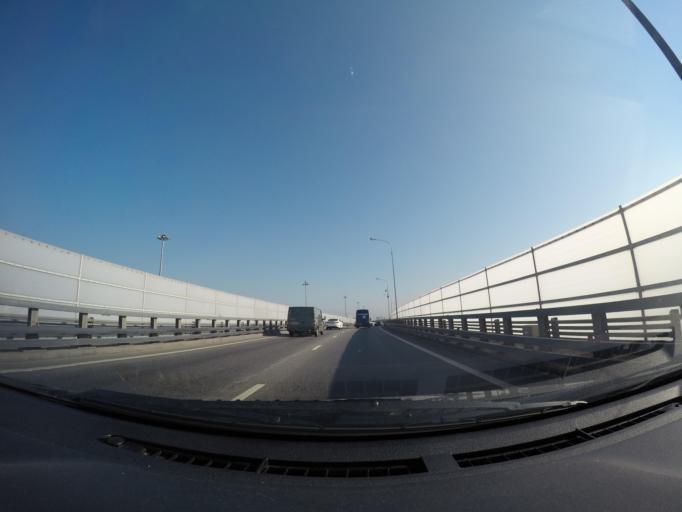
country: RU
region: Moscow
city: Ryazanskiy
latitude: 55.7525
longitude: 37.7469
